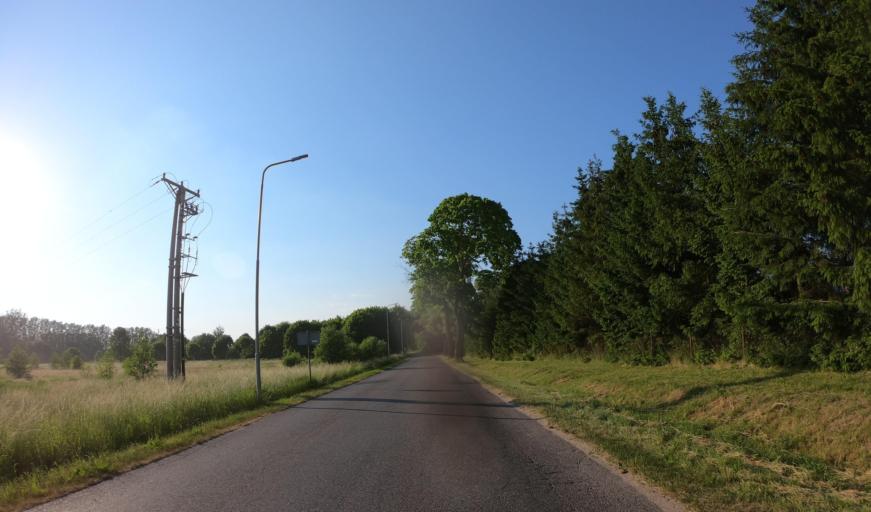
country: PL
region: West Pomeranian Voivodeship
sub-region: Powiat lobeski
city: Resko
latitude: 53.7601
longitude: 15.4091
